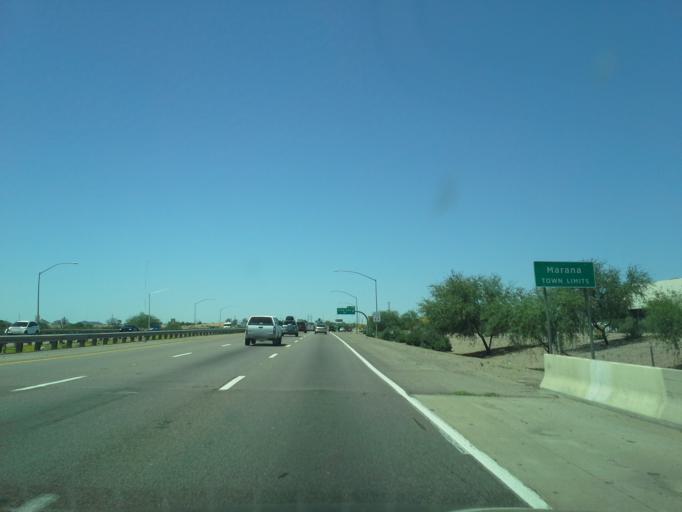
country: US
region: Arizona
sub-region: Pima County
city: Flowing Wells
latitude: 32.3154
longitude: -111.0461
